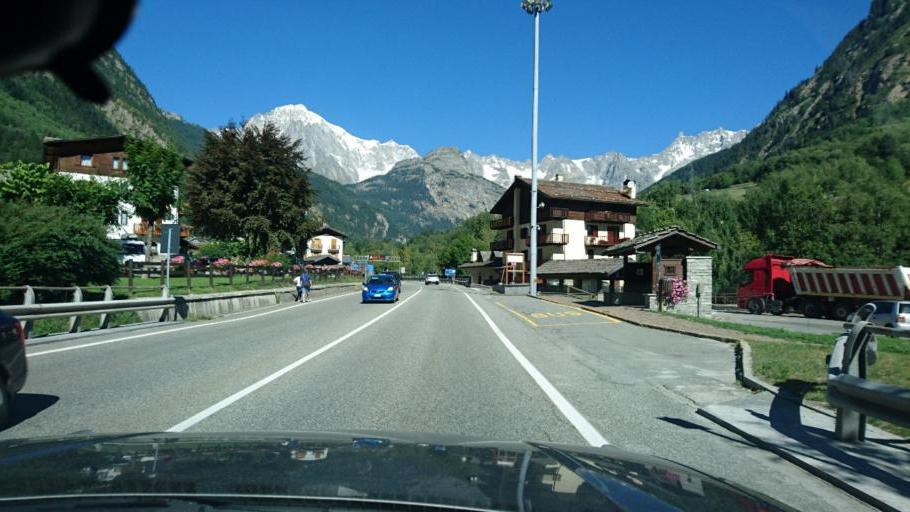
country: IT
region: Aosta Valley
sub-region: Valle d'Aosta
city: Pre Saint Didier
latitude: 45.7629
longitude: 6.9898
